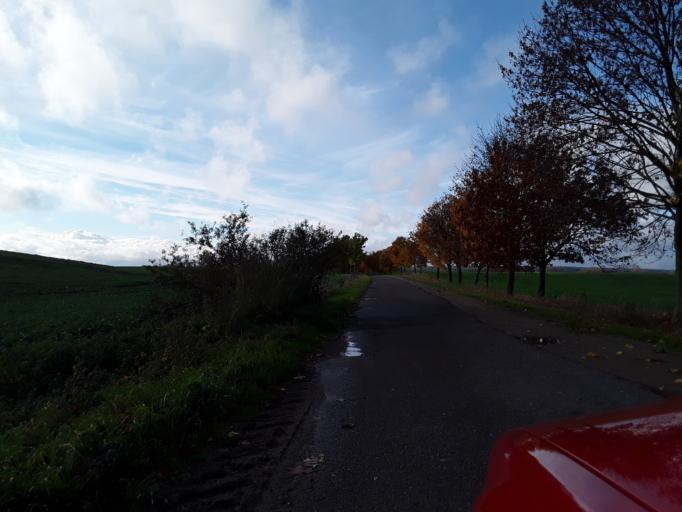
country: DE
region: Brandenburg
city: Mittenwalde
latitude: 53.2810
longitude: 13.7231
